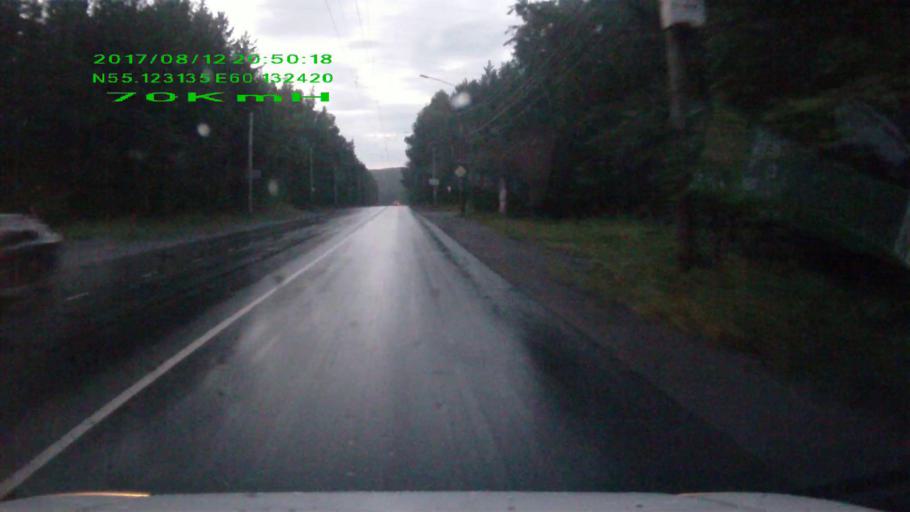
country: RU
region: Chelyabinsk
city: Turgoyak
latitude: 55.1233
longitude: 60.1325
